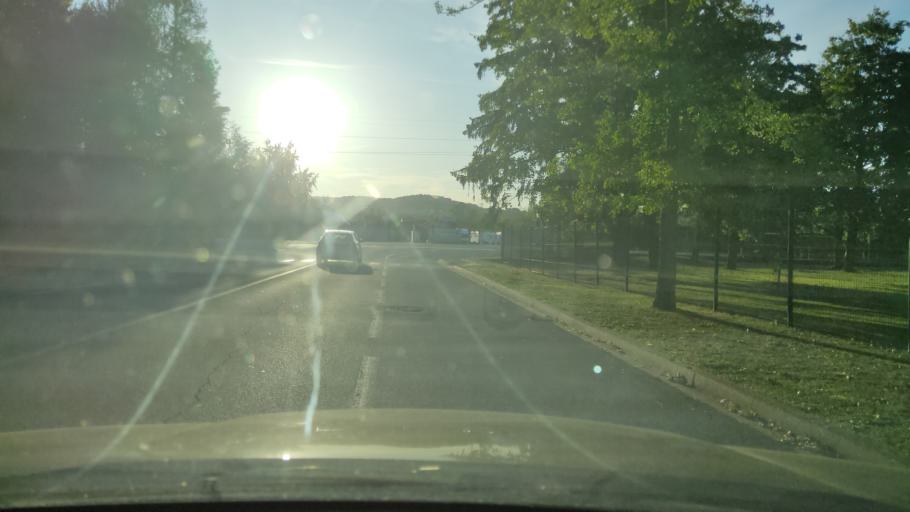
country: FR
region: Lorraine
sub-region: Departement de la Moselle
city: Maizieres-les-Metz
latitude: 49.1984
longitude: 6.1505
